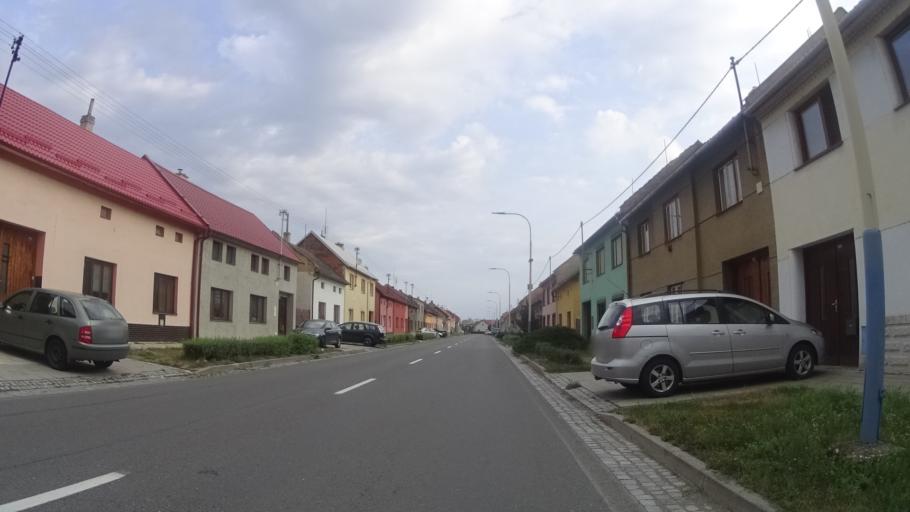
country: CZ
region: Zlin
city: Chropyne
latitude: 49.3529
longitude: 17.3748
